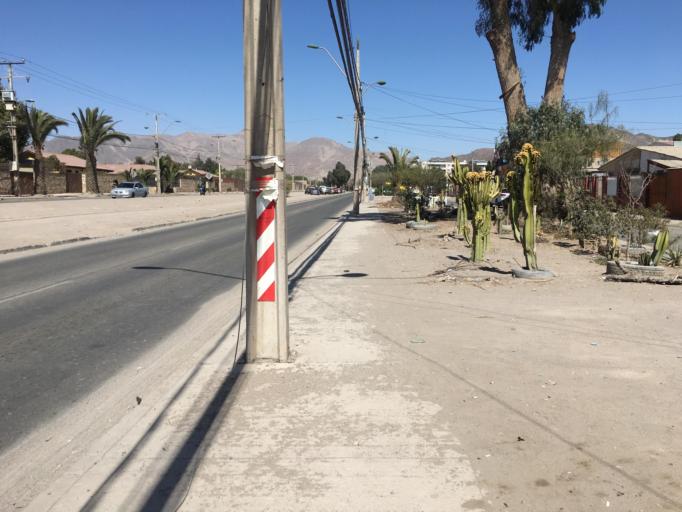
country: CL
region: Atacama
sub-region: Provincia de Copiapo
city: Copiapo
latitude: -27.4086
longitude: -70.2867
